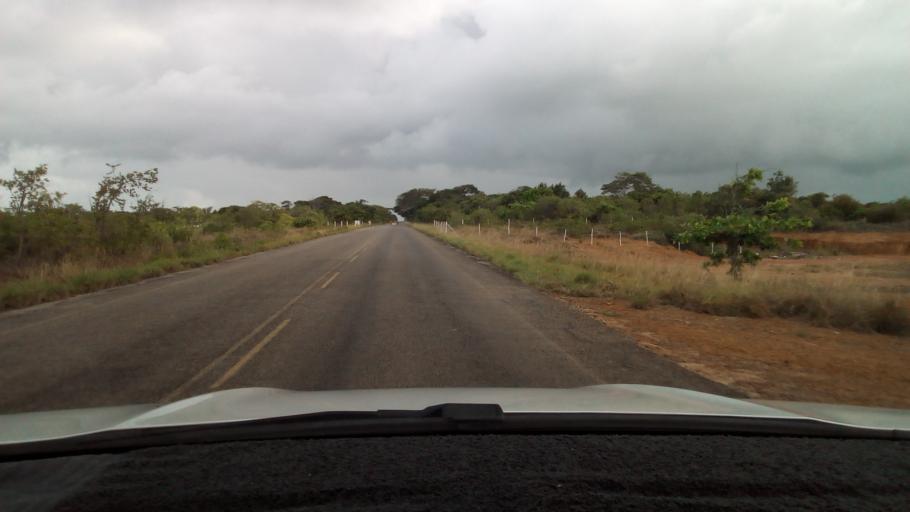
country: BR
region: Paraiba
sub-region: Conde
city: Conde
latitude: -7.3232
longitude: -34.8081
